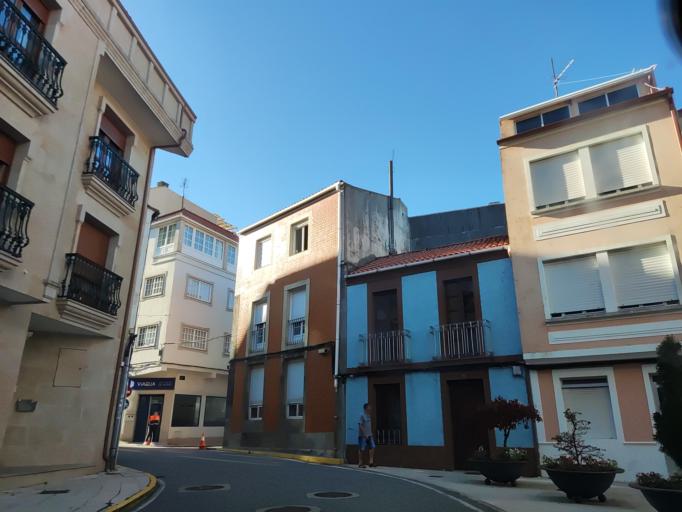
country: ES
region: Galicia
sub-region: Provincia da Coruna
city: Boiro
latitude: 42.6028
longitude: -8.9382
